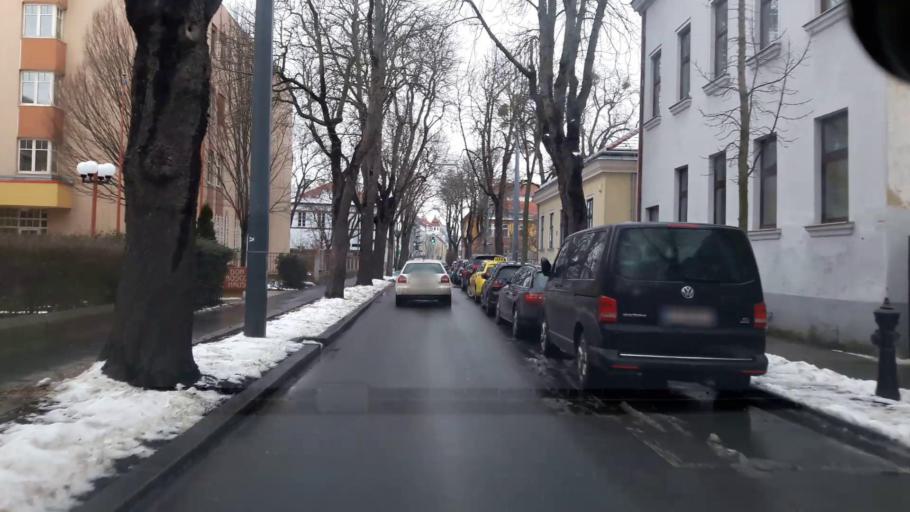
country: AT
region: Lower Austria
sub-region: Politischer Bezirk Modling
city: Perchtoldsdorf
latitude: 48.1860
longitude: 16.2842
